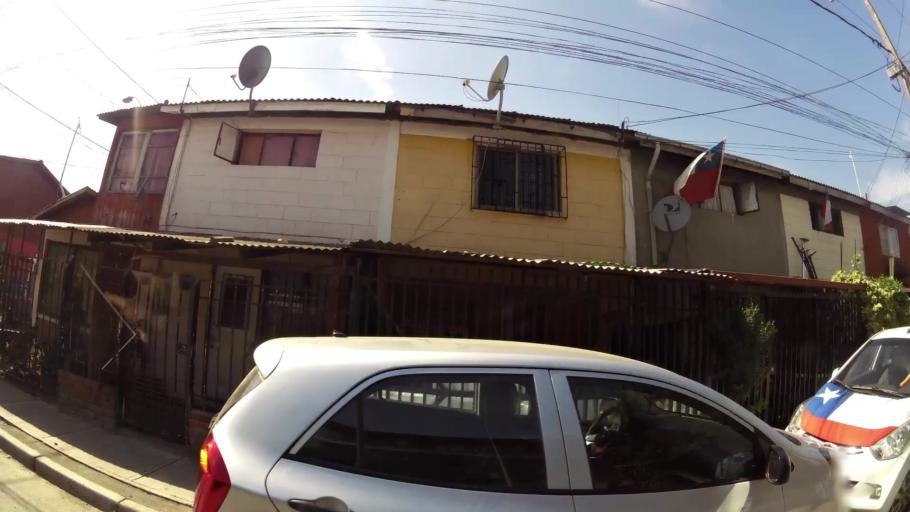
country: CL
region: Santiago Metropolitan
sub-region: Provincia de Santiago
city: La Pintana
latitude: -33.5618
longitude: -70.6407
